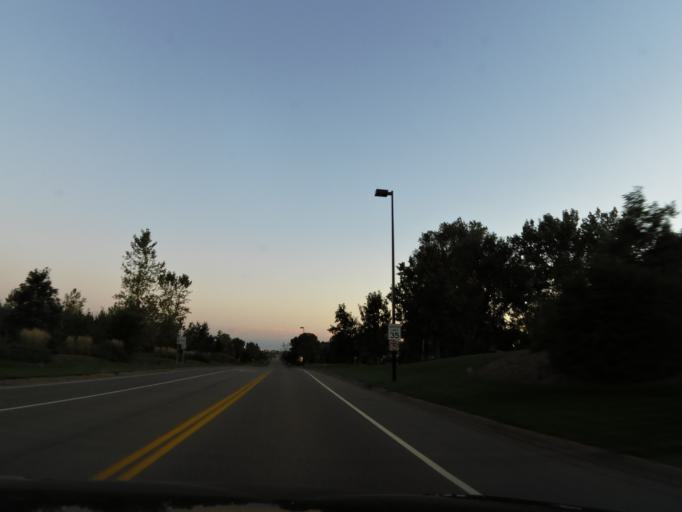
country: US
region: Minnesota
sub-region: Washington County
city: Oakdale
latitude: 44.9588
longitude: -92.9646
